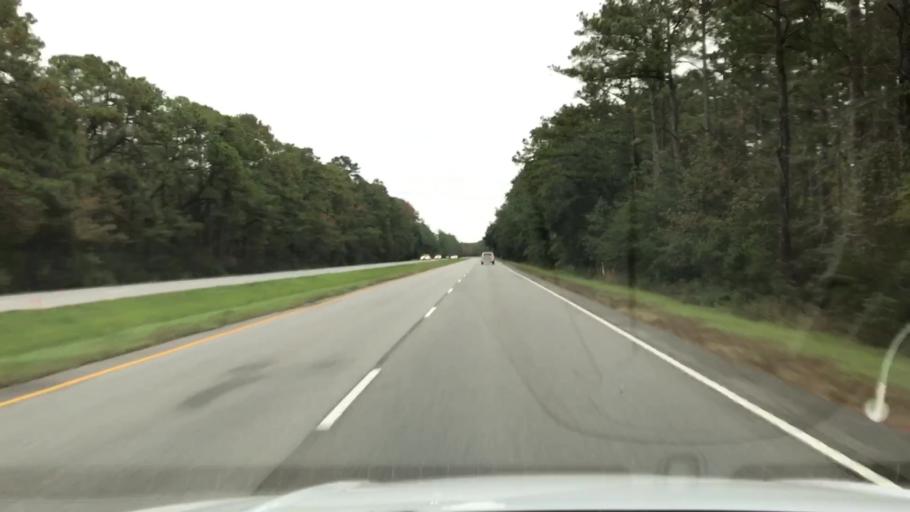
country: US
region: South Carolina
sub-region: Georgetown County
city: Georgetown
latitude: 33.3949
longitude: -79.2023
